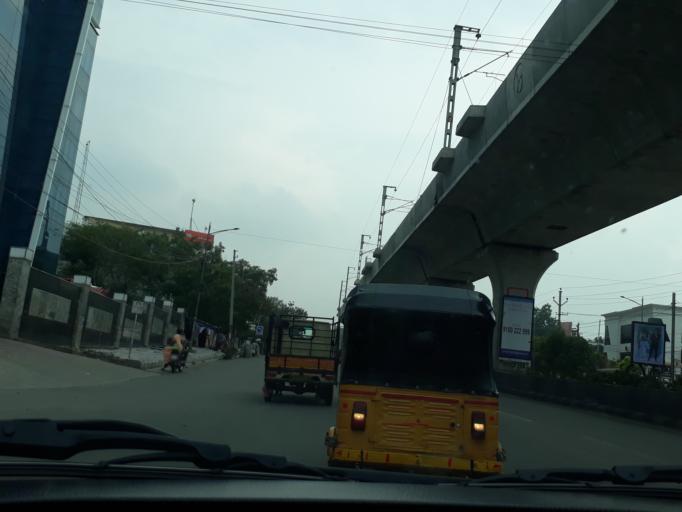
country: IN
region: Telangana
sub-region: Rangareddi
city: Kukatpalli
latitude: 17.4284
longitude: 78.4174
